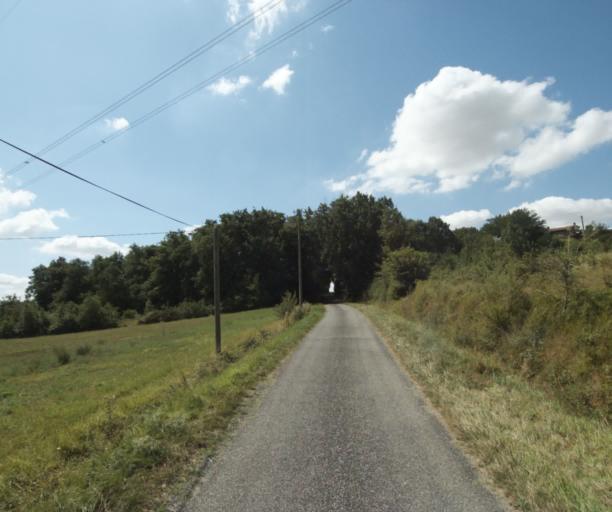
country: FR
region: Midi-Pyrenees
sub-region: Departement de la Haute-Garonne
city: Auriac-sur-Vendinelle
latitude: 43.4764
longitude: 1.7968
